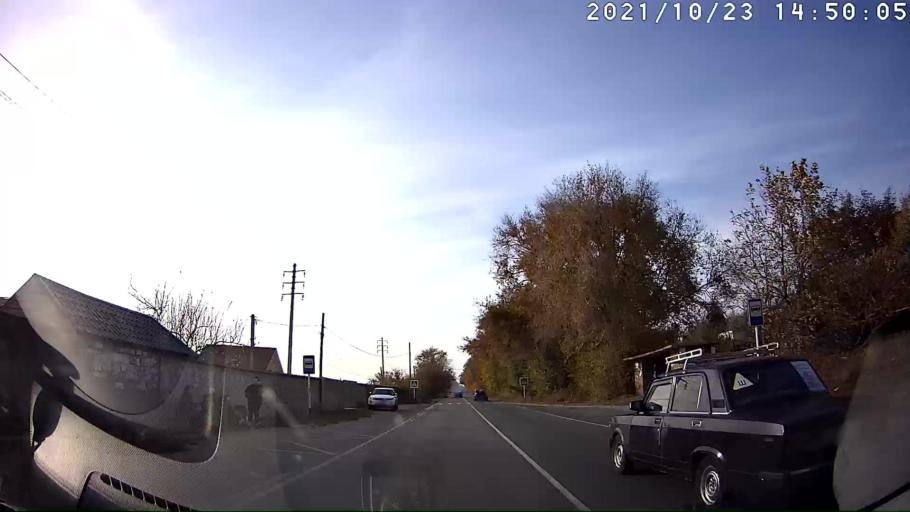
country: RU
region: Volgograd
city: Volgograd
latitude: 48.4291
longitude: 44.4756
